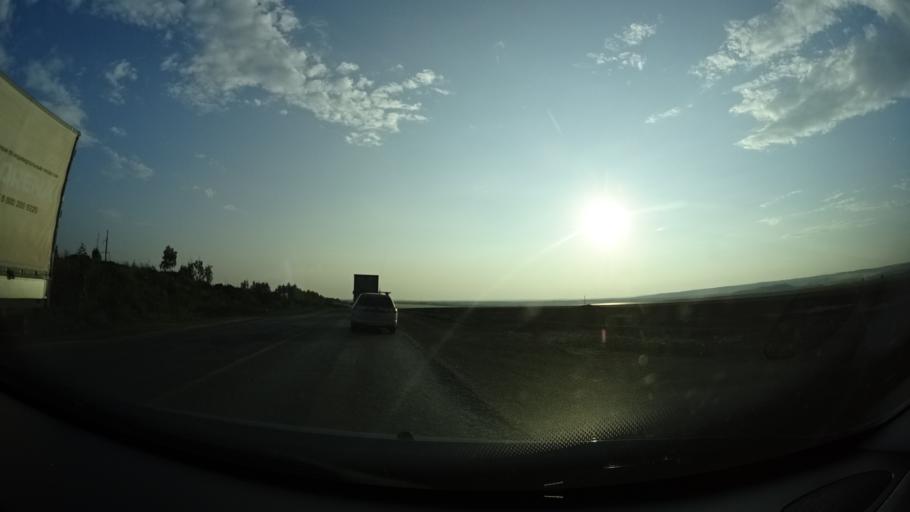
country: RU
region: Samara
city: Kamyshla
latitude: 54.0436
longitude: 51.9952
